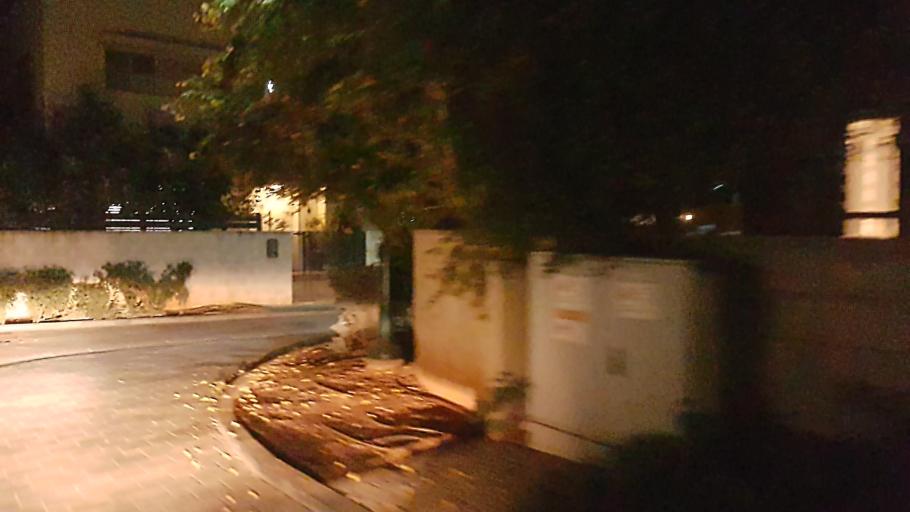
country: IL
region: Central District
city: Hod HaSharon
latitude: 32.1634
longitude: 34.8904
